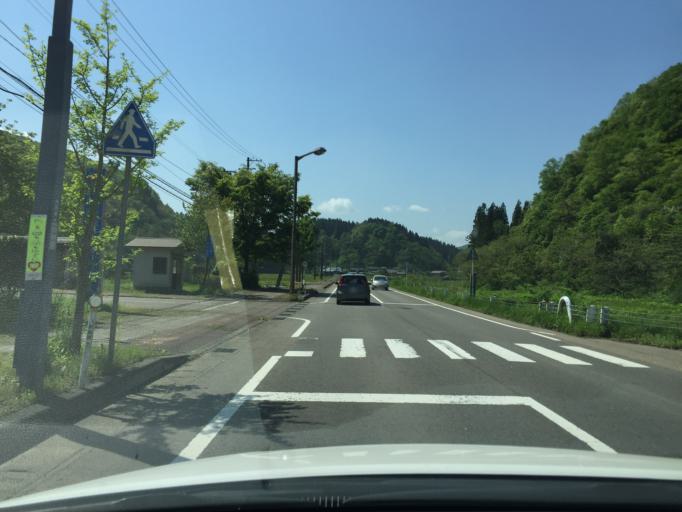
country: JP
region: Niigata
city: Kamo
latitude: 37.6233
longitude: 139.1041
